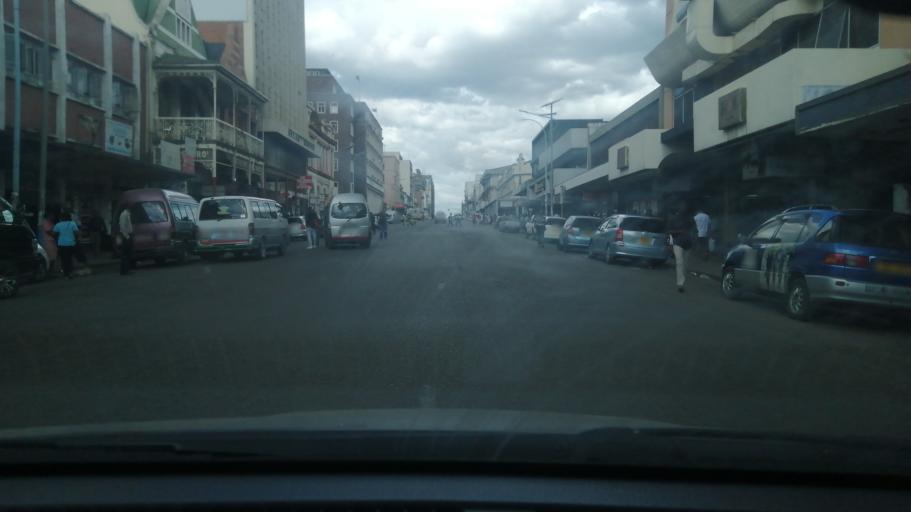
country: ZW
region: Harare
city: Harare
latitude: -17.8331
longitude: 31.0472
